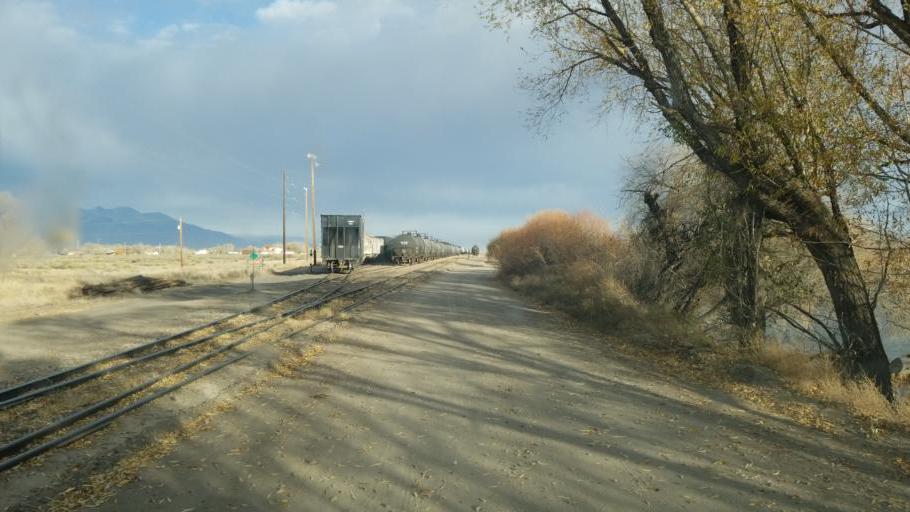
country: US
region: Colorado
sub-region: Alamosa County
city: Alamosa East
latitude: 37.4664
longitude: -105.8473
